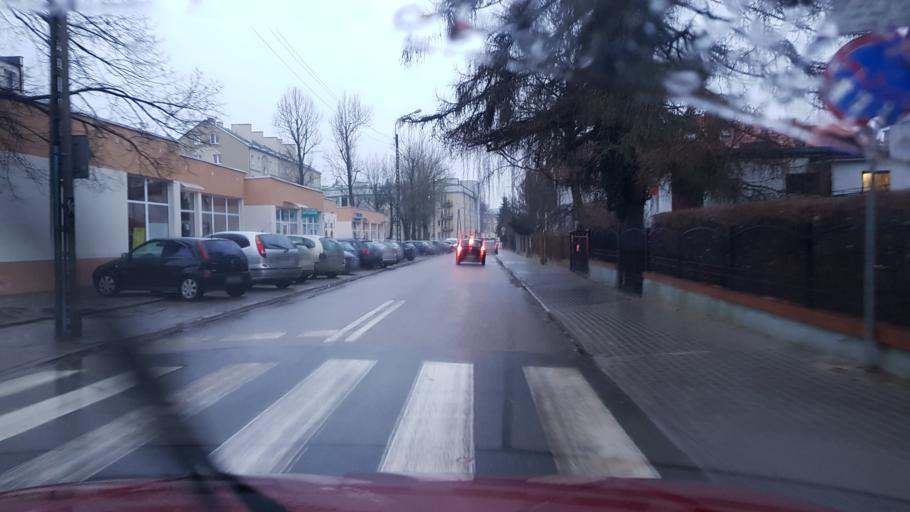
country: PL
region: West Pomeranian Voivodeship
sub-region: Koszalin
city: Koszalin
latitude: 54.1932
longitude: 16.2038
